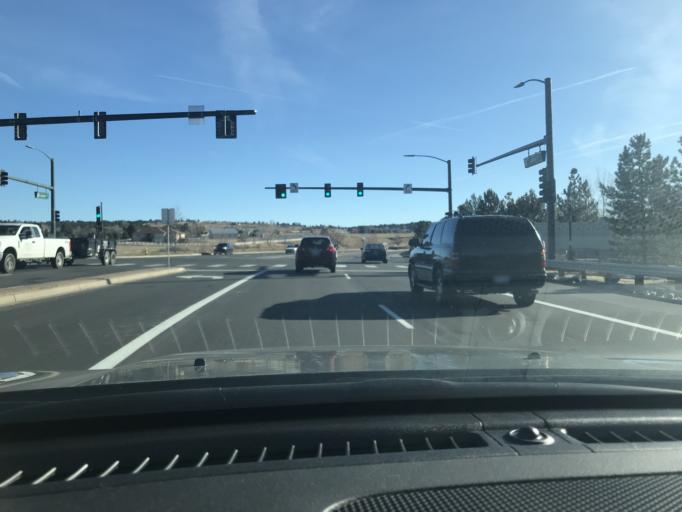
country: US
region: Colorado
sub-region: Douglas County
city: Parker
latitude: 39.5373
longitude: -104.7661
